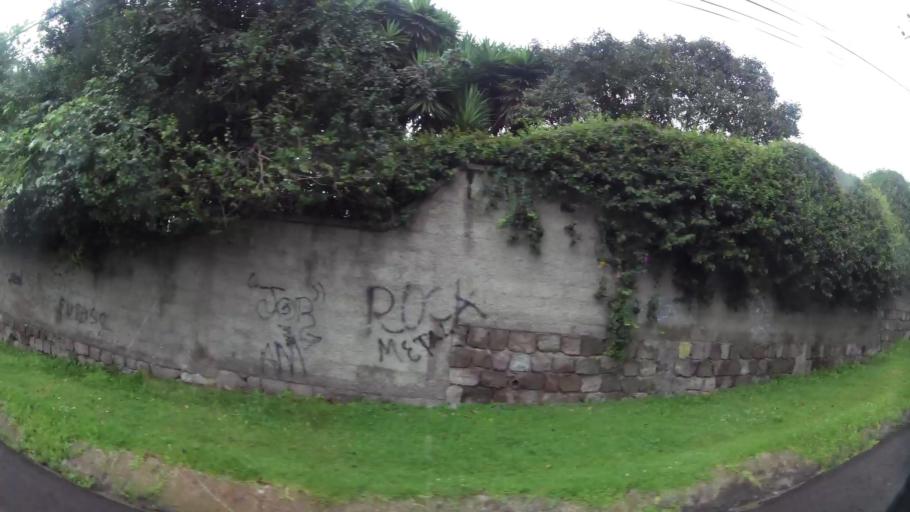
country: EC
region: Pichincha
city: Sangolqui
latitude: -0.2798
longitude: -78.4598
